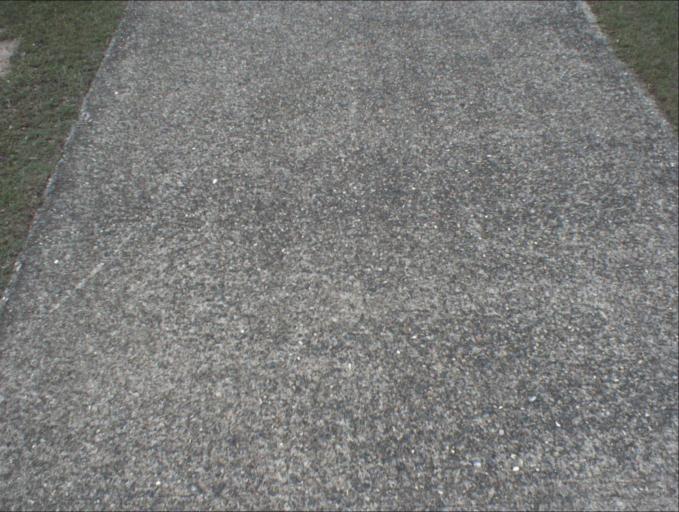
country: AU
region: Queensland
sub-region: Logan
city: Logan Reserve
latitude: -27.6843
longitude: 153.0800
